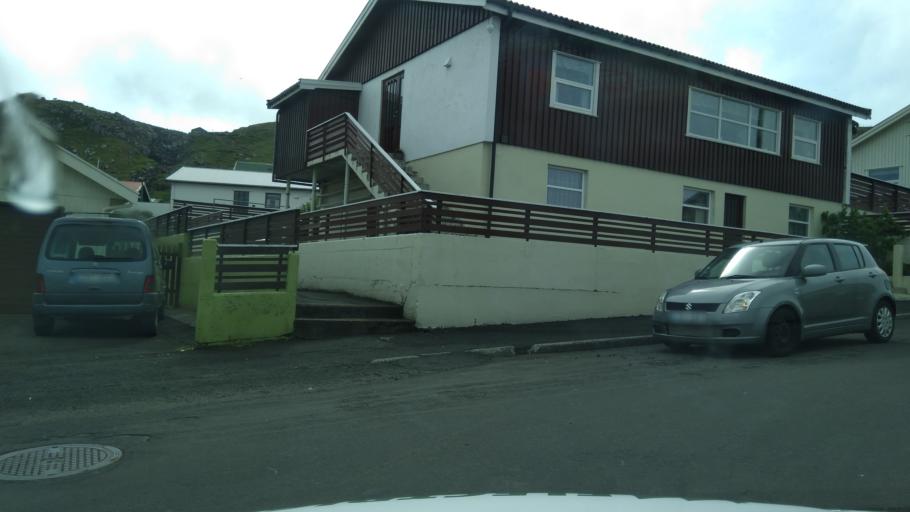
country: FO
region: Sandoy
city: Sandur
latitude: 61.9032
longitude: -6.8893
